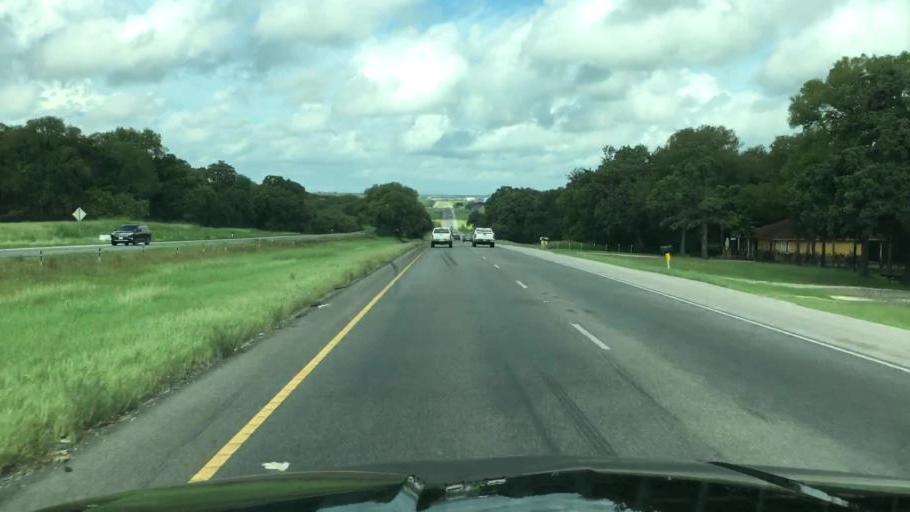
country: US
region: Texas
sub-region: Bastrop County
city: Wyldwood
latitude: 30.1530
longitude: -97.4910
